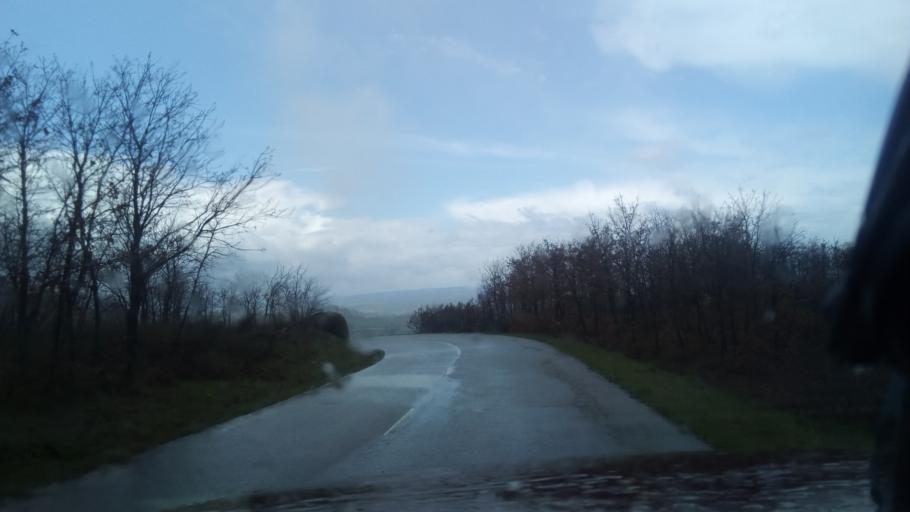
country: PT
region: Guarda
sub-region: Fornos de Algodres
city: Fornos de Algodres
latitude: 40.5535
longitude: -7.4697
